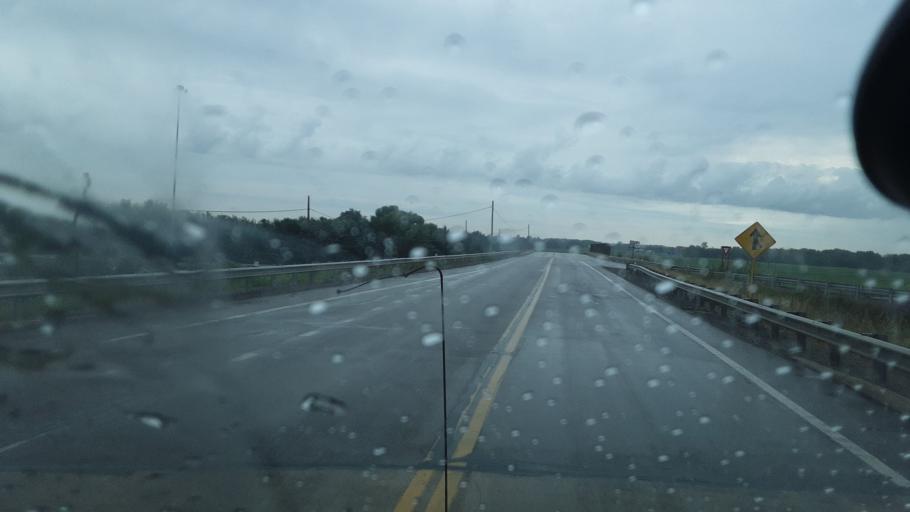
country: US
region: Ohio
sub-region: Williams County
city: Montpelier
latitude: 41.6130
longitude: -84.5550
